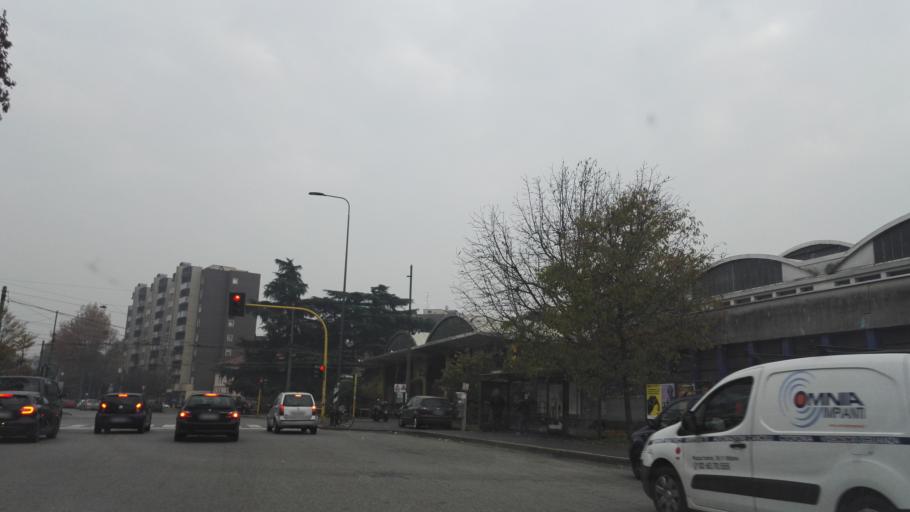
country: IT
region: Lombardy
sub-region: Citta metropolitana di Milano
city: Romano Banco
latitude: 45.4703
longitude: 9.1230
